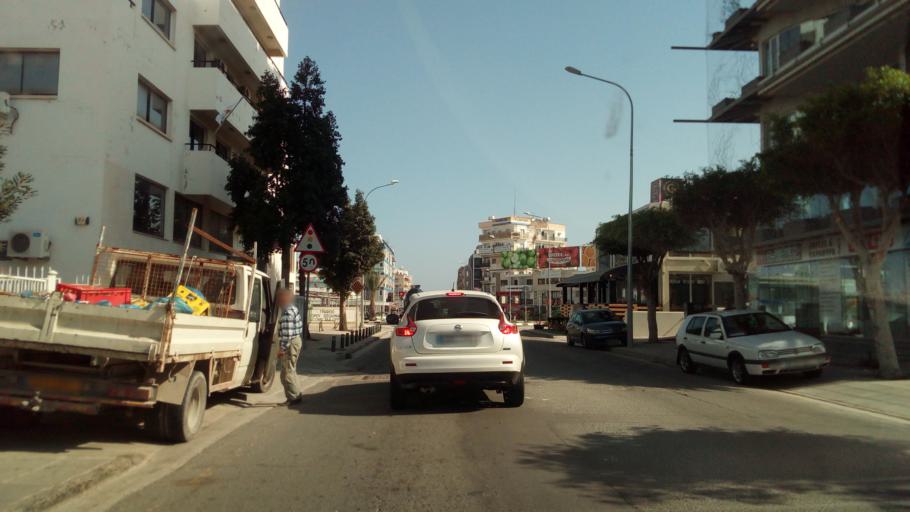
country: CY
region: Larnaka
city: Larnaca
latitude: 34.9209
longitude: 33.6155
